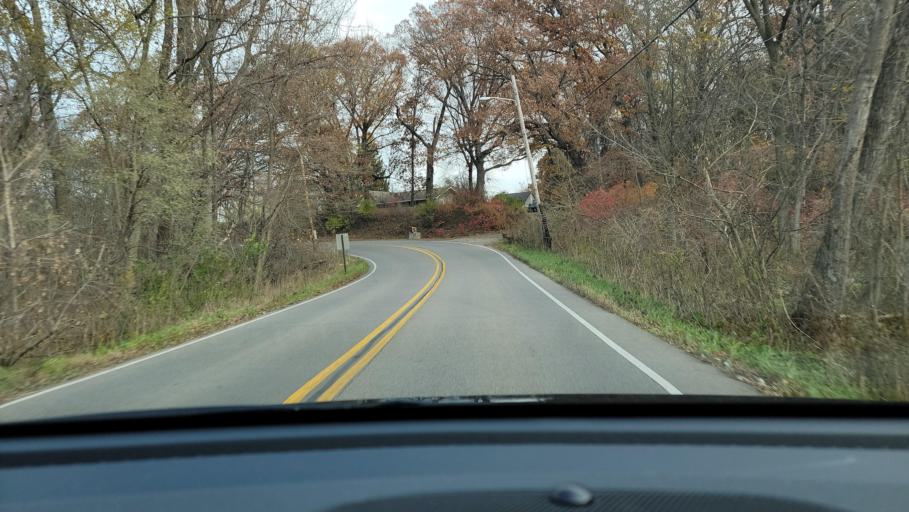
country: US
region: Indiana
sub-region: Porter County
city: Portage
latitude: 41.5839
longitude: -87.1368
